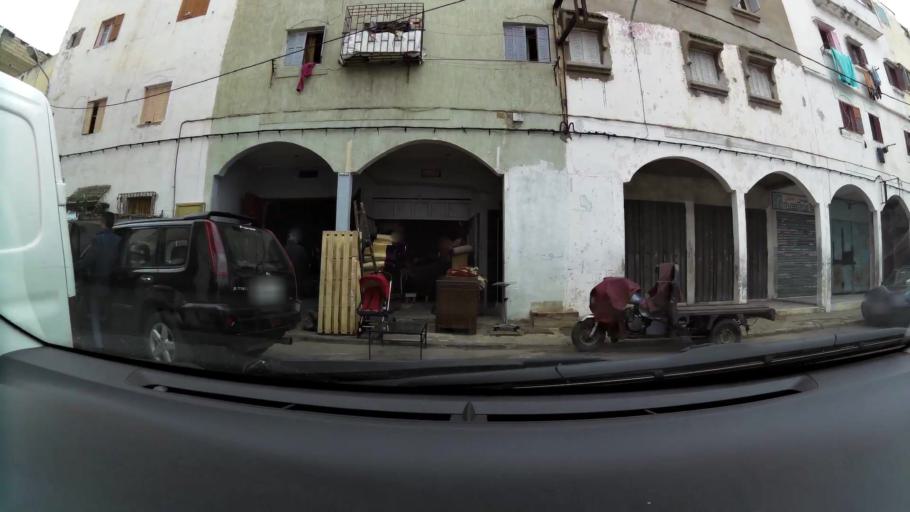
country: MA
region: Grand Casablanca
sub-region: Casablanca
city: Casablanca
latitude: 33.5872
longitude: -7.5506
